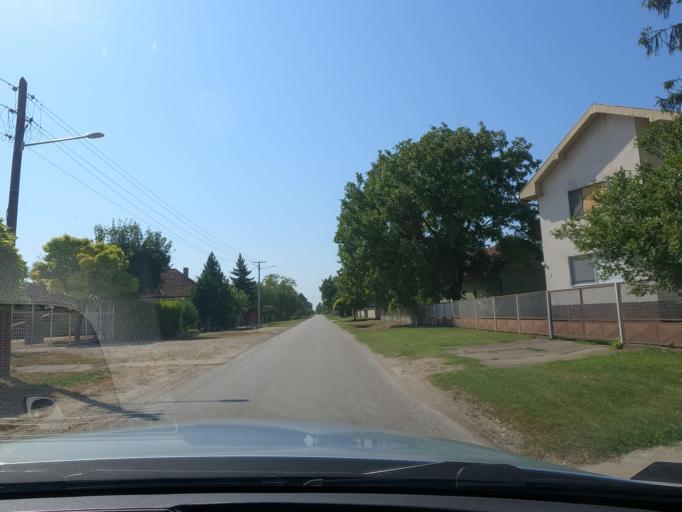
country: HU
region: Csongrad
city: Asotthalom
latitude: 46.0985
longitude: 19.7790
